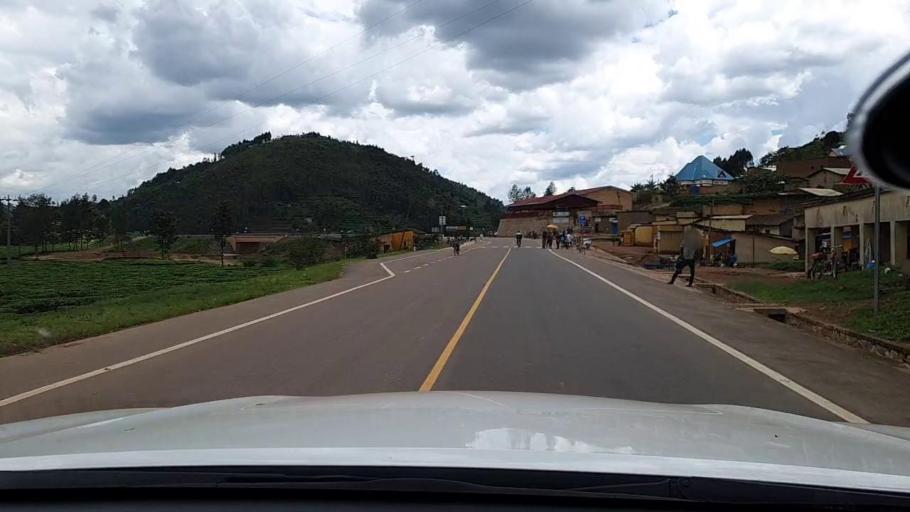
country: RW
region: Northern Province
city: Byumba
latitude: -1.6544
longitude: 29.9063
